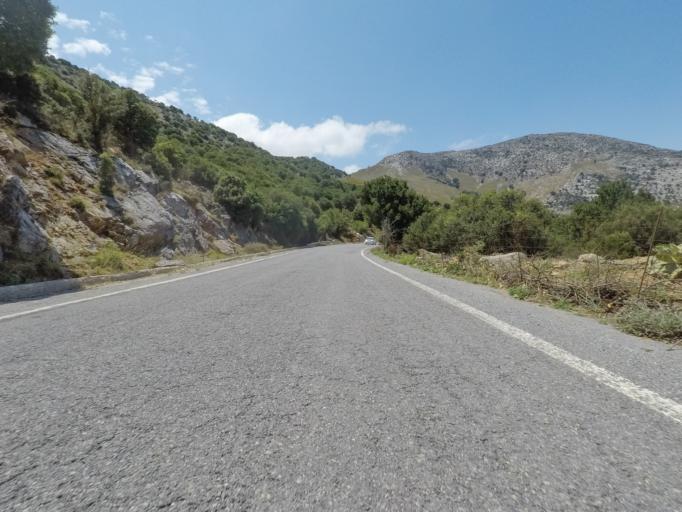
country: GR
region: Crete
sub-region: Nomos Irakleiou
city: Mokhos
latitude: 35.1779
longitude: 25.4357
